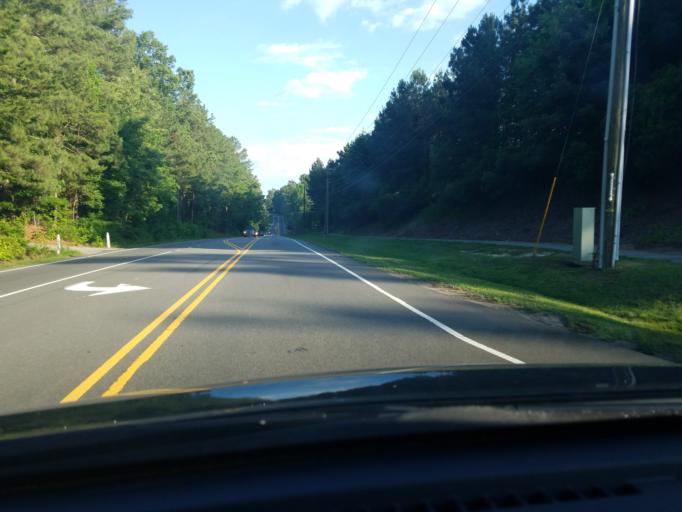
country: US
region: North Carolina
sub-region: Durham County
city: Durham
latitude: 35.9417
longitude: -78.9658
